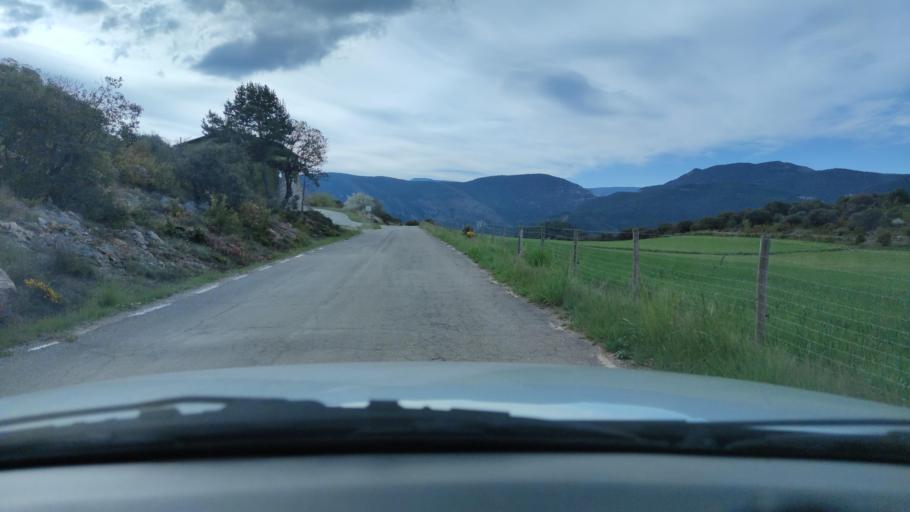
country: ES
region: Catalonia
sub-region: Provincia de Lleida
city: Coll de Nargo
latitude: 42.2390
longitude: 1.3795
